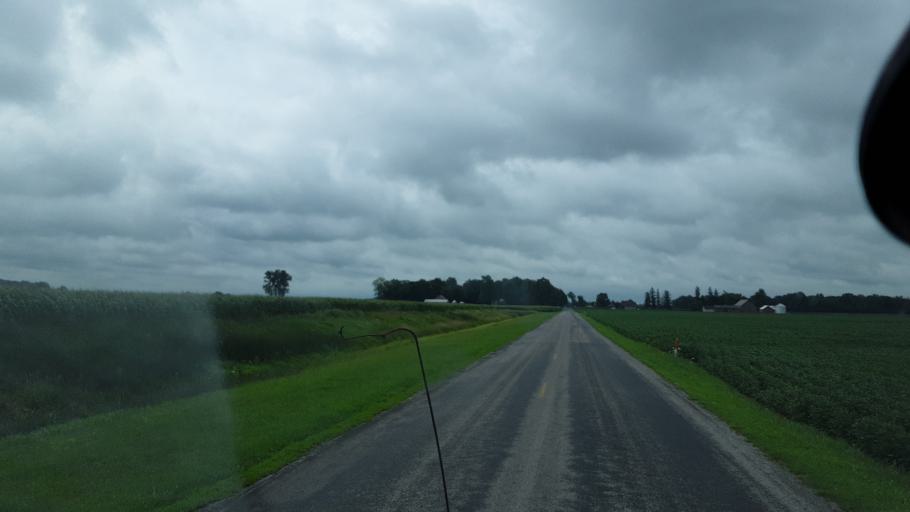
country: US
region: Indiana
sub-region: Wells County
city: Ossian
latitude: 40.8655
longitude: -85.1093
